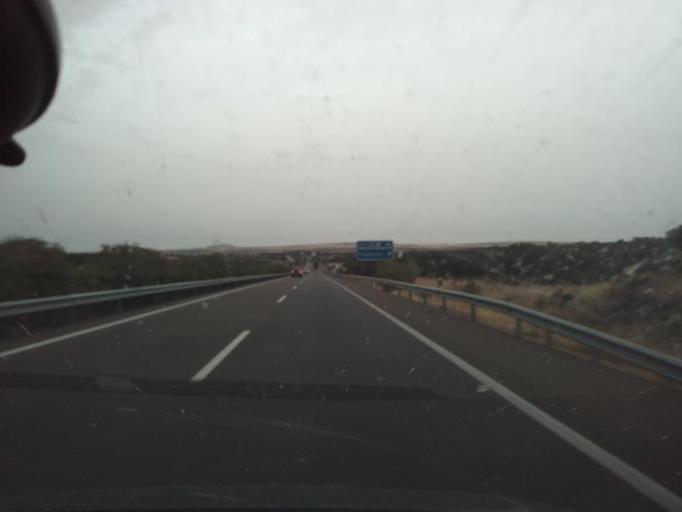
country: ES
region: Extremadura
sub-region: Provincia de Badajoz
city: Trujillanos
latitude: 38.9521
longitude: -6.2331
